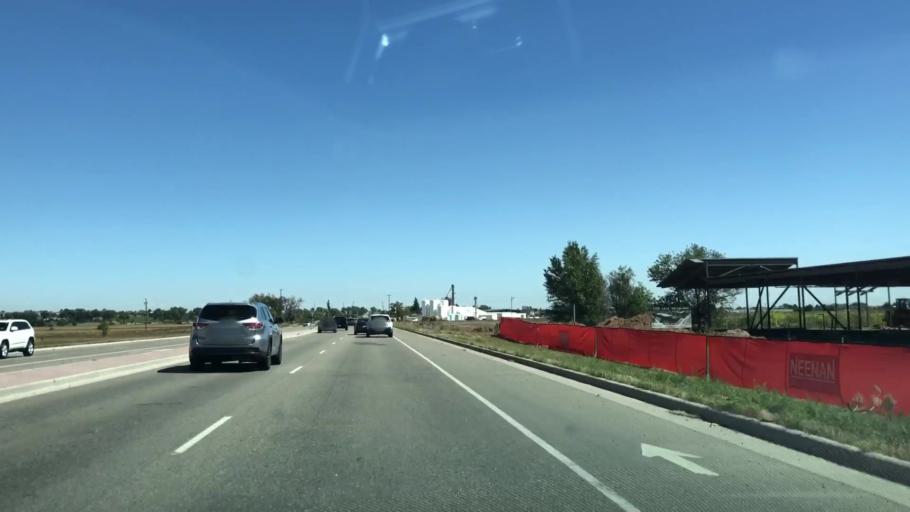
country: US
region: Colorado
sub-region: Weld County
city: Windsor
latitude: 40.5229
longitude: -104.9765
